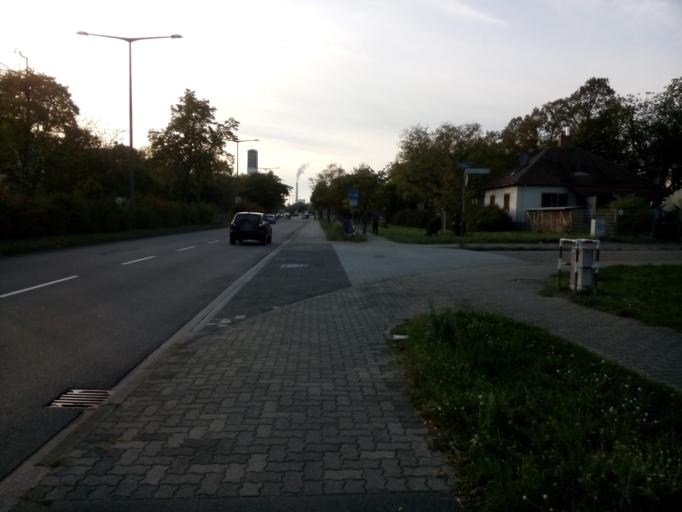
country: DE
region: Baden-Wuerttemberg
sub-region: Karlsruhe Region
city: Karlsruhe
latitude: 48.9981
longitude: 8.3544
